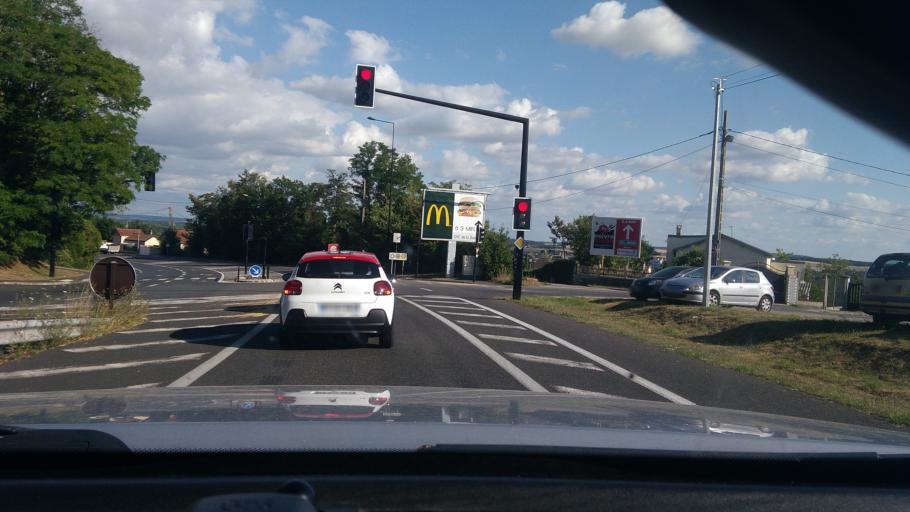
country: FR
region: Ile-de-France
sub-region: Departement de Seine-et-Marne
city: Montereau-Fault-Yonne
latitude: 48.3920
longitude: 2.9480
